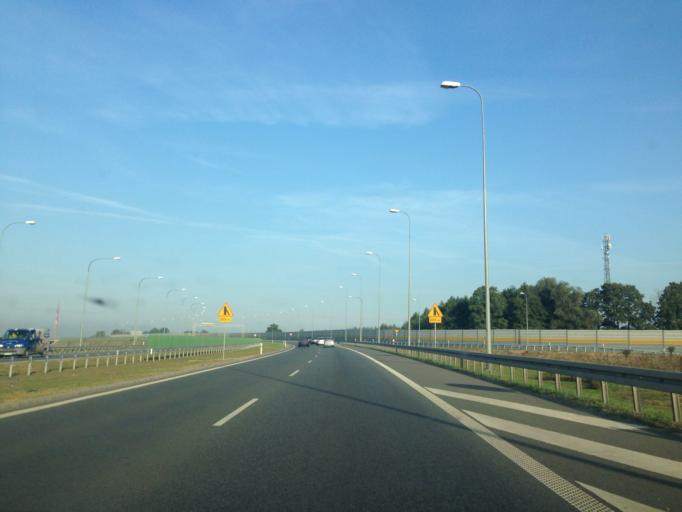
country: PL
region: Kujawsko-Pomorskie
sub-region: Powiat torunski
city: Lubicz Dolny
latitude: 53.0361
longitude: 18.7425
